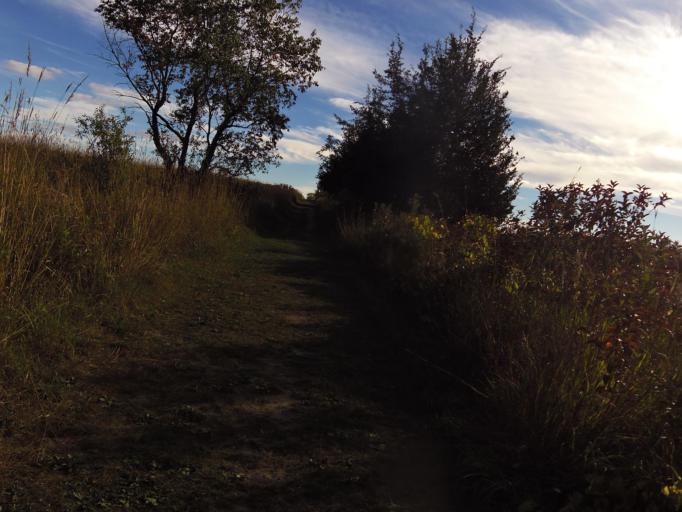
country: US
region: Minnesota
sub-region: Washington County
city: Afton
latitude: 44.8700
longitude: -92.7916
